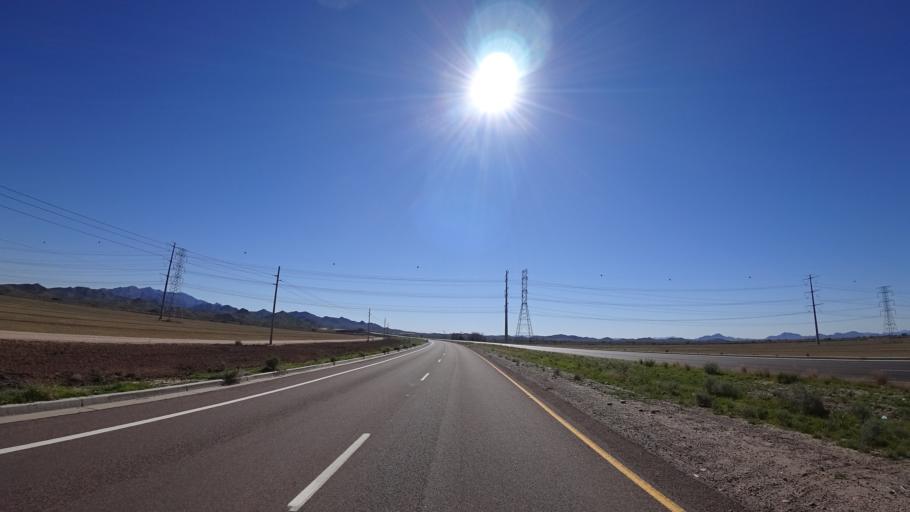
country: US
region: Arizona
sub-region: Maricopa County
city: Goodyear
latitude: 33.3965
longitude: -112.4269
